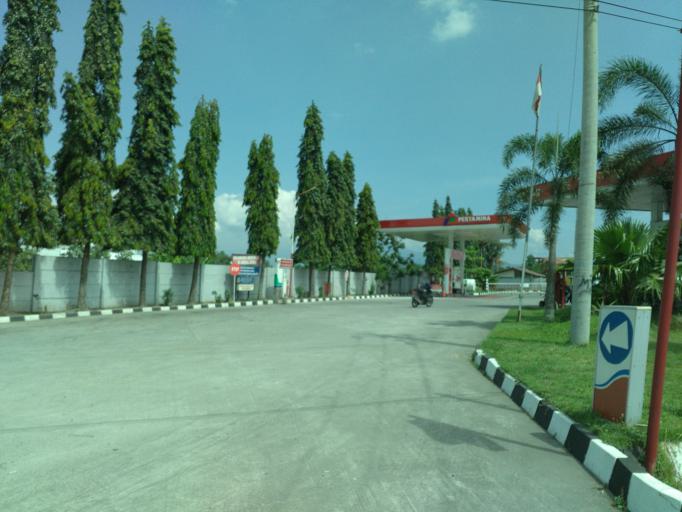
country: ID
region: Central Java
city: Candi Prambanan
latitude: -7.7478
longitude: 110.5235
